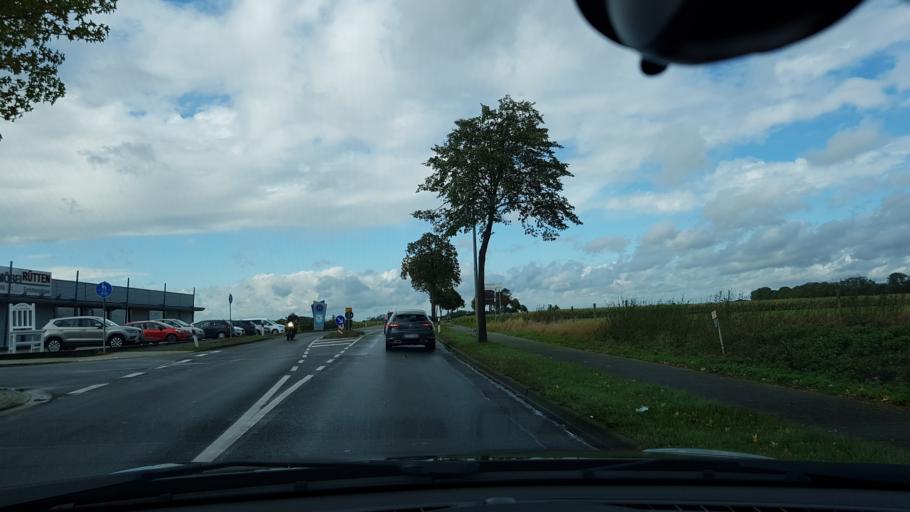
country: DE
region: North Rhine-Westphalia
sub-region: Regierungsbezirk Koln
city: Wassenberg
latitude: 51.0722
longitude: 6.1803
